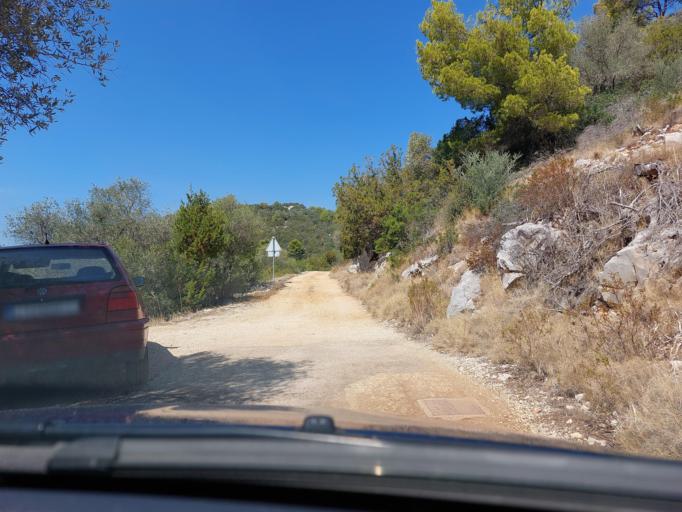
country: HR
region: Dubrovacko-Neretvanska
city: Smokvica
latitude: 42.7733
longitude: 16.8380
